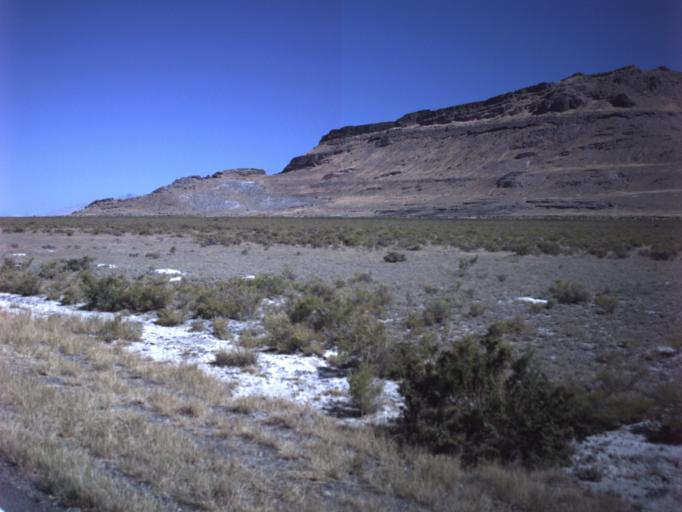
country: US
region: Utah
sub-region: Tooele County
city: Grantsville
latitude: 40.7252
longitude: -112.6589
